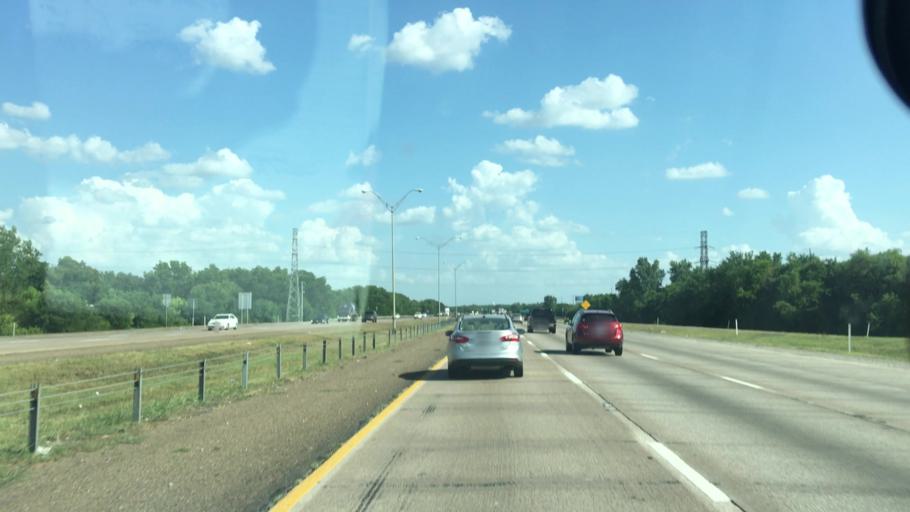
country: US
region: Texas
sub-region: Dallas County
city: Hutchins
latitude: 32.6981
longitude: -96.7520
